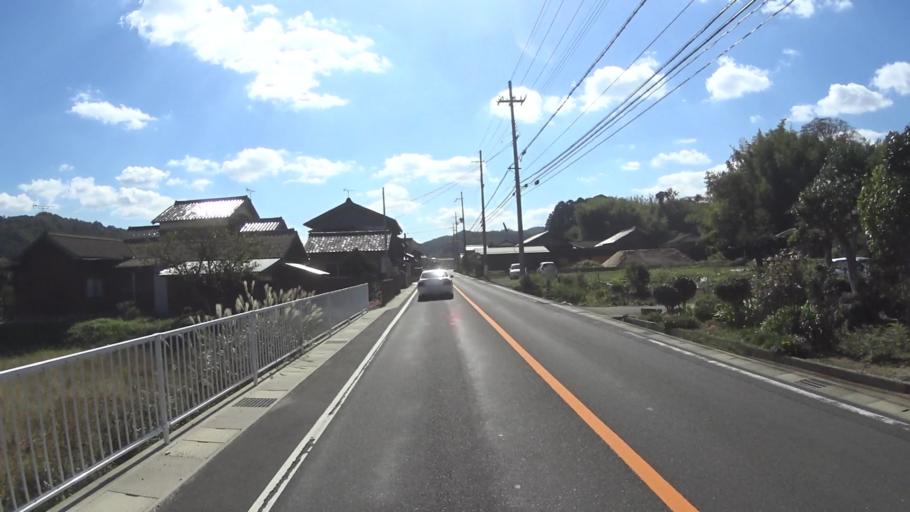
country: JP
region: Kyoto
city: Miyazu
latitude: 35.6586
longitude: 135.0320
